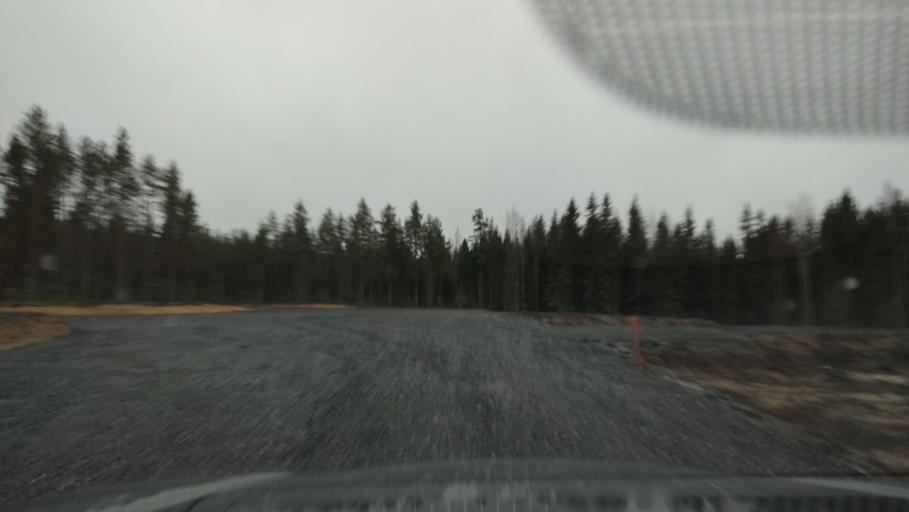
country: FI
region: Southern Ostrobothnia
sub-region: Suupohja
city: Karijoki
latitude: 62.1443
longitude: 21.6133
